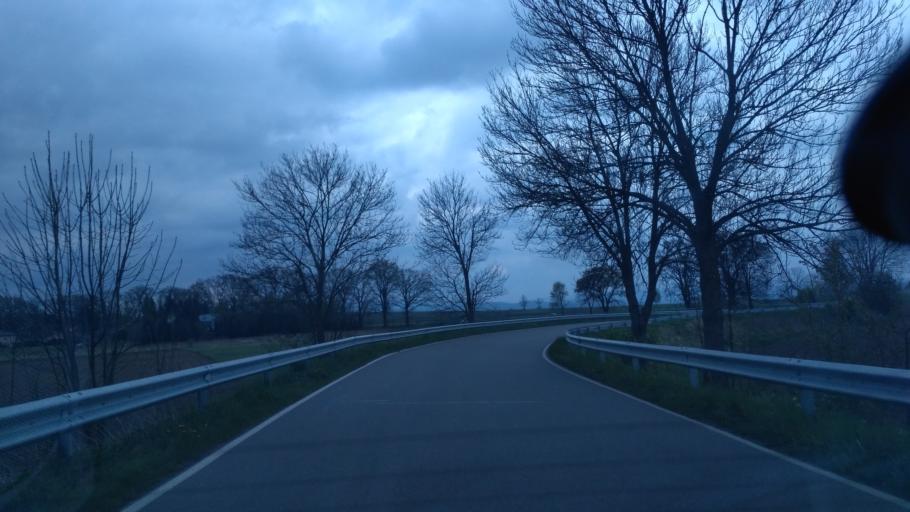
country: PL
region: Subcarpathian Voivodeship
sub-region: Powiat brzozowski
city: Turze Pole
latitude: 49.6515
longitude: 21.9939
